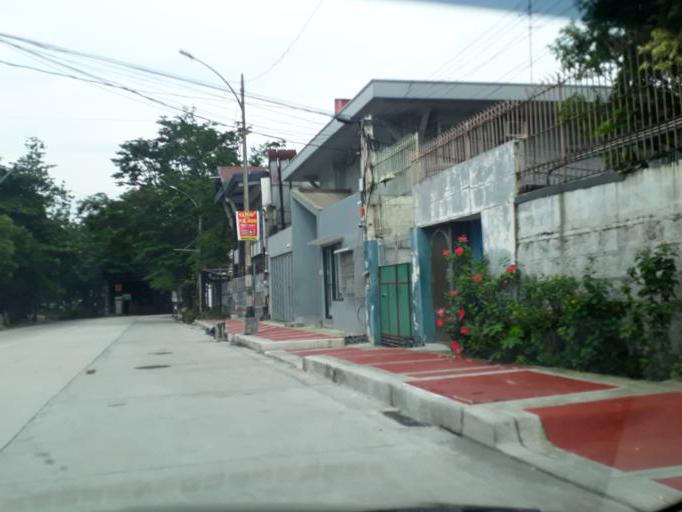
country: PH
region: Calabarzon
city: Del Monte
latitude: 14.6321
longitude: 121.0227
